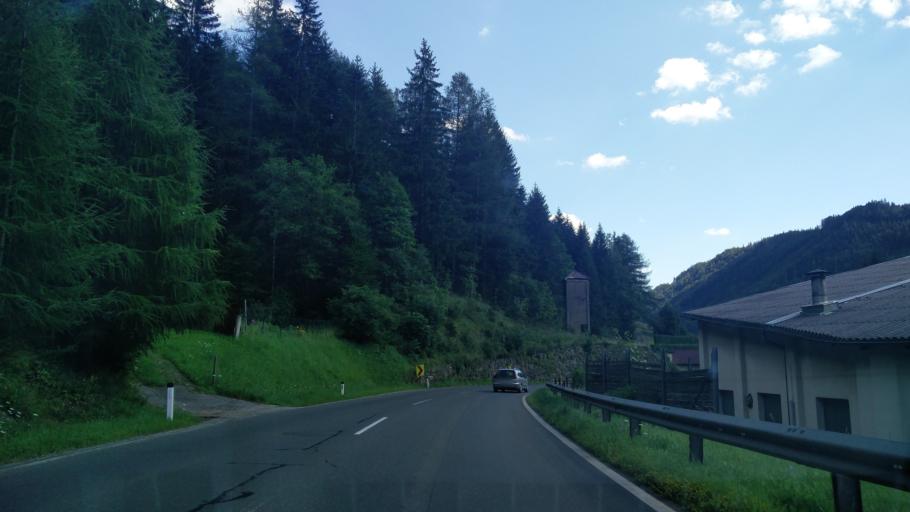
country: AT
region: Styria
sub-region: Politischer Bezirk Leoben
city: Vordernberg
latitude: 47.4715
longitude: 14.9888
